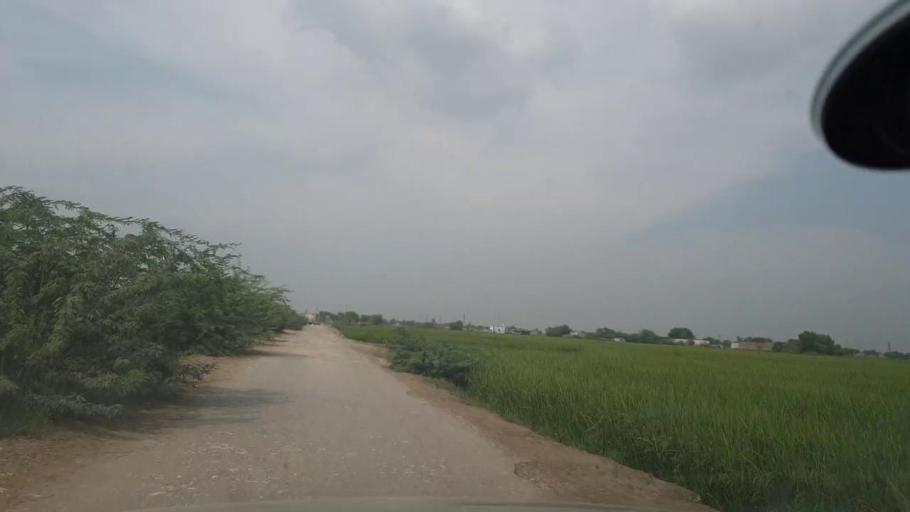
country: PK
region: Sindh
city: Jacobabad
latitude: 28.2542
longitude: 68.4370
